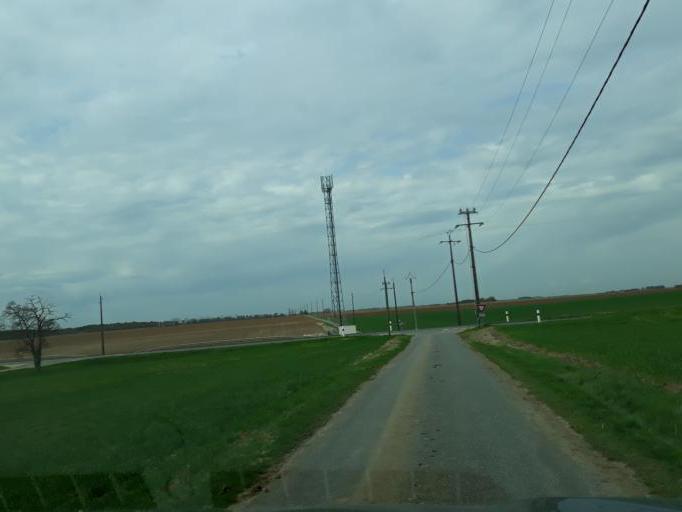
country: FR
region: Centre
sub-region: Departement du Loiret
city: Epieds-en-Beauce
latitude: 47.9354
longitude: 1.6076
